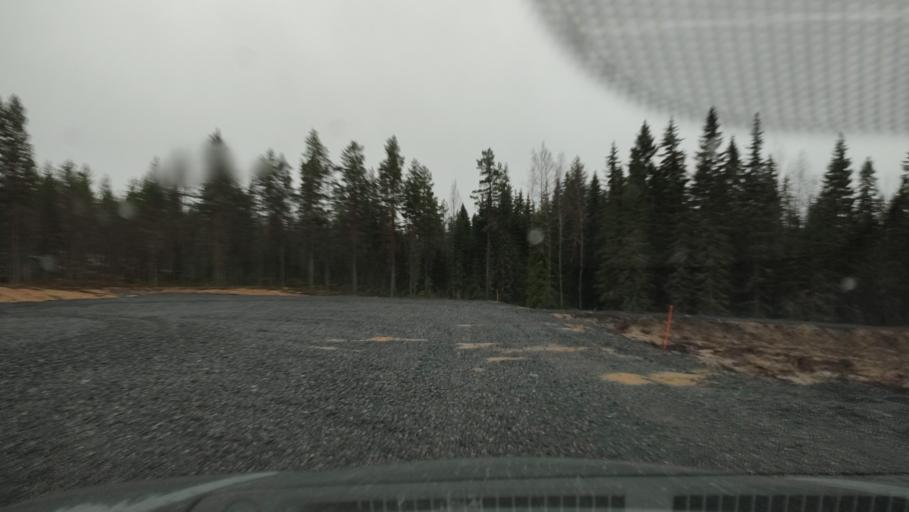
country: FI
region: Southern Ostrobothnia
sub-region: Suupohja
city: Karijoki
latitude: 62.1439
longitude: 21.6133
